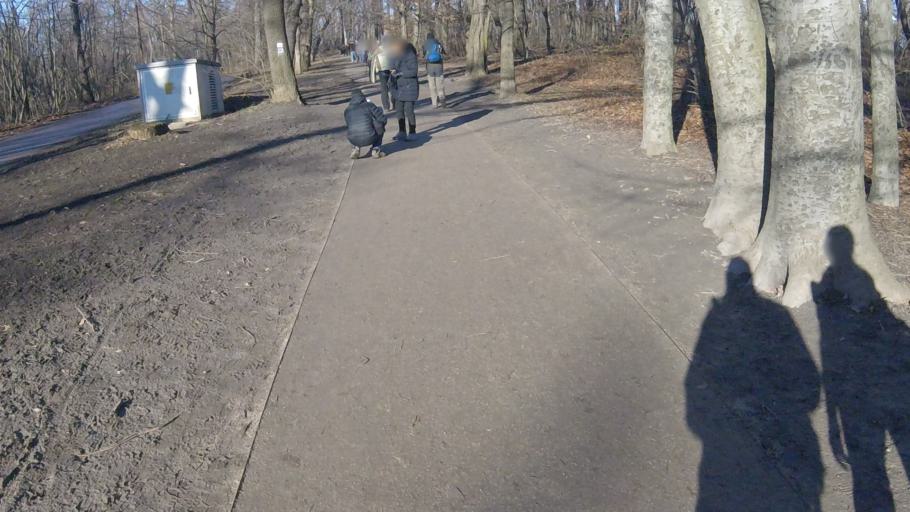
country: HU
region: Pest
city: Budakeszi
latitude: 47.5073
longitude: 18.9598
